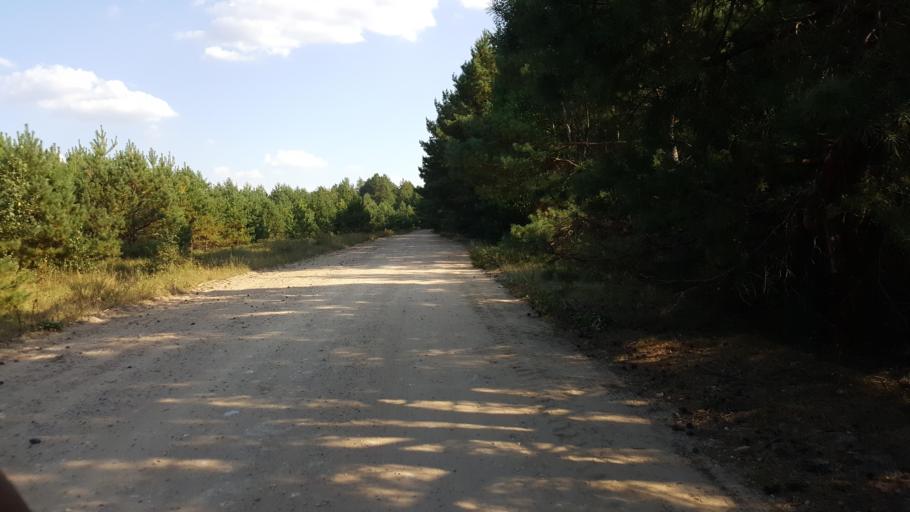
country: BY
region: Brest
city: Kamyanyuki
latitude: 52.5589
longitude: 23.6431
